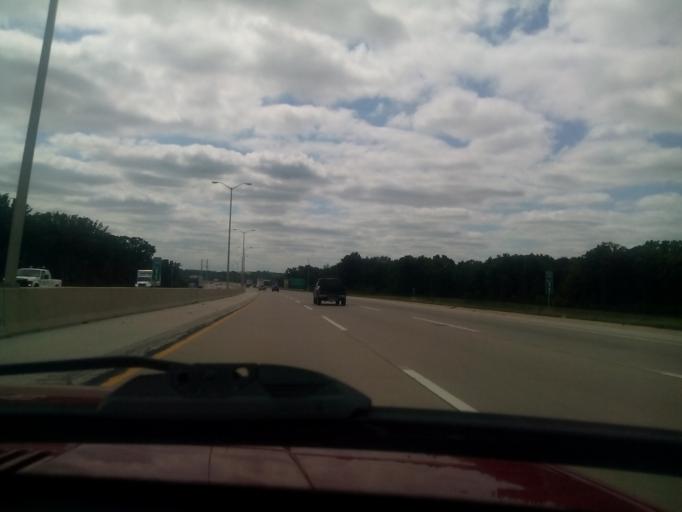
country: US
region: Illinois
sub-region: Cook County
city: Lemont
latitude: 41.6848
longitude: -88.0306
